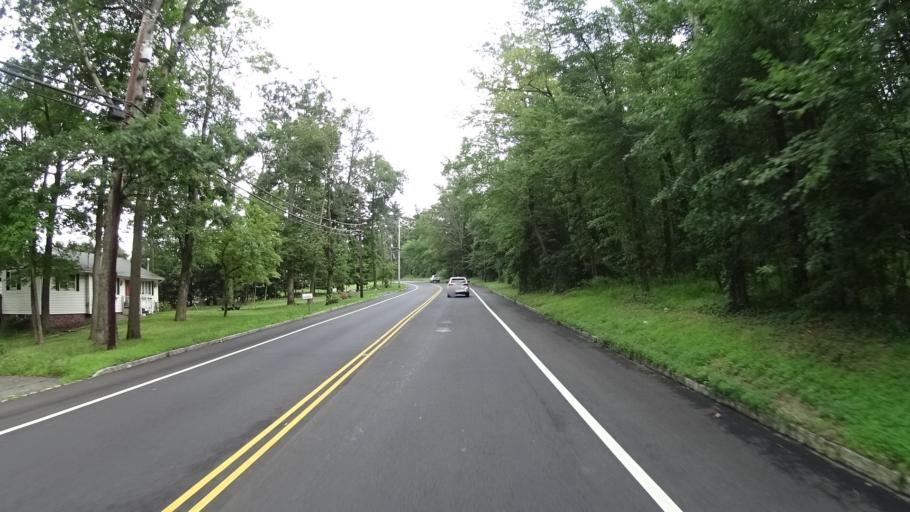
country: US
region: New Jersey
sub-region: Somerset County
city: Warren Township
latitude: 40.6362
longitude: -74.5124
